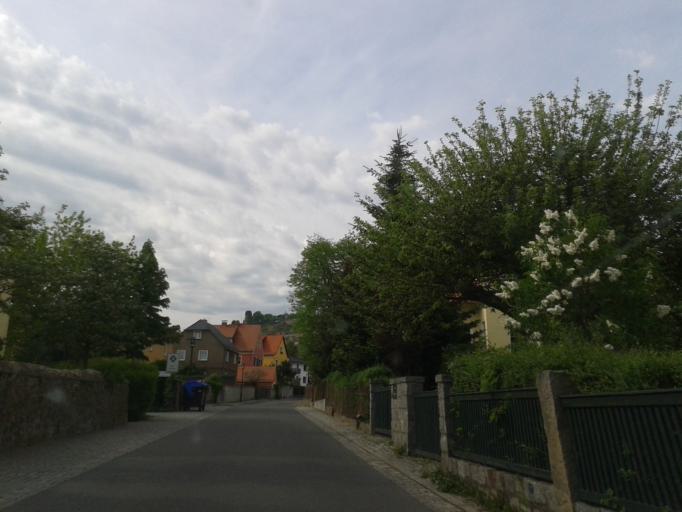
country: DE
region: Saxony
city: Radebeul
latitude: 51.1073
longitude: 13.6714
